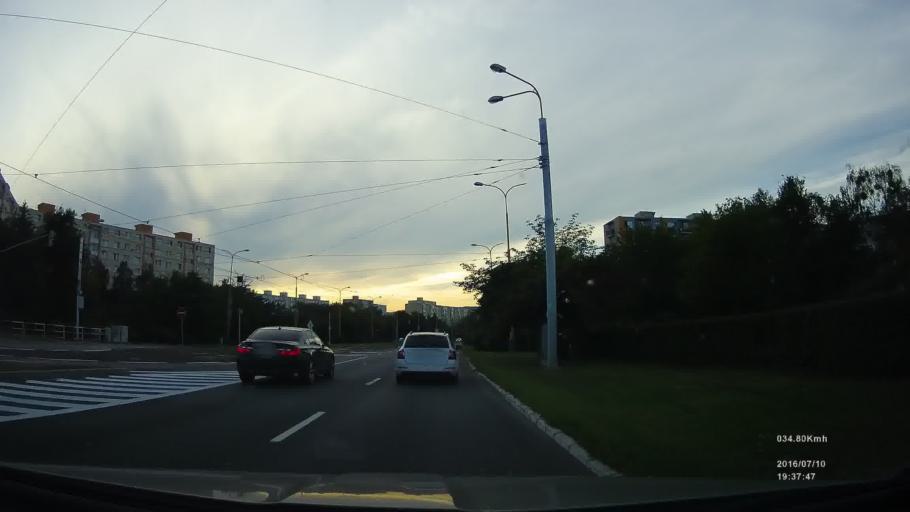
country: SK
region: Kosicky
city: Kosice
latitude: 48.7071
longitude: 21.2395
